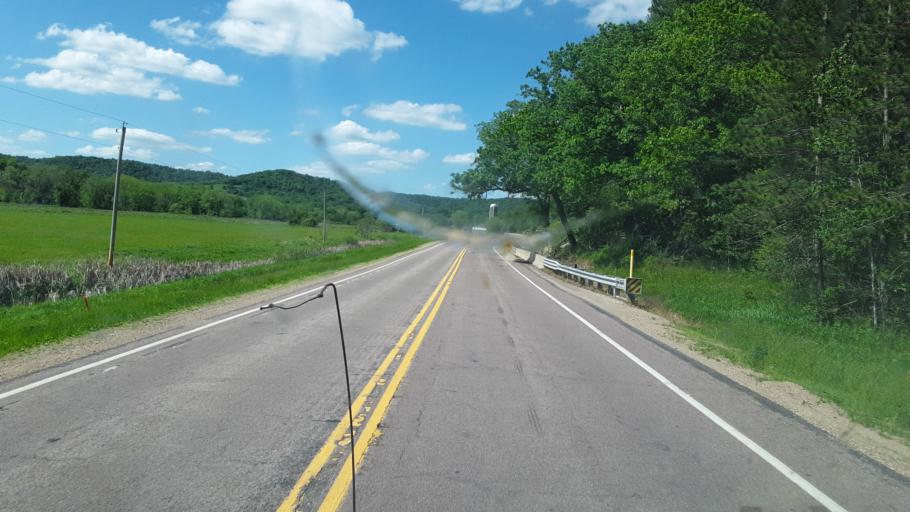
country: US
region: Wisconsin
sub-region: Richland County
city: Richland Center
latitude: 43.3633
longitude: -90.2656
